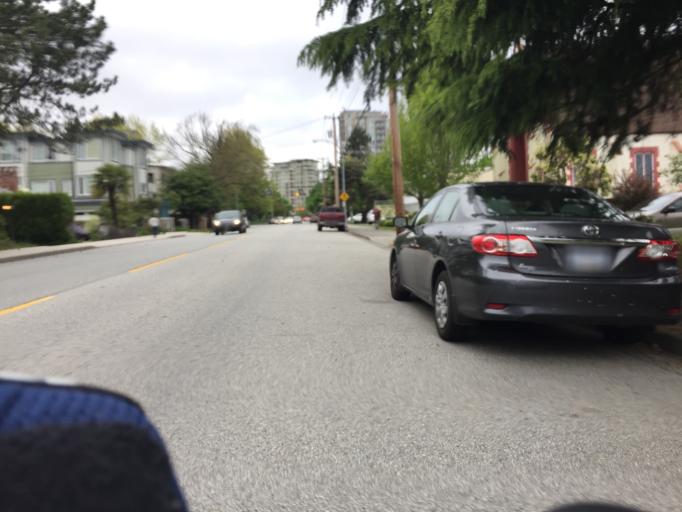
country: CA
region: British Columbia
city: Richmond
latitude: 49.1598
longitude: -123.1309
